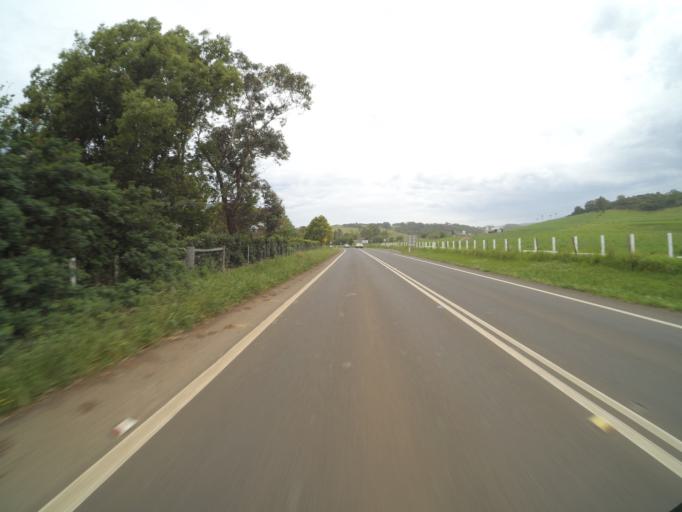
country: AU
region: New South Wales
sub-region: Kiama
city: Jamberoo
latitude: -34.6493
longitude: 150.7908
